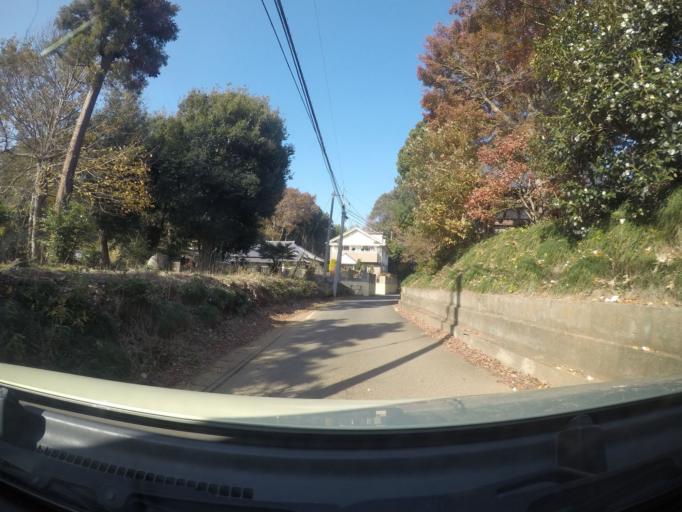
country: JP
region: Ibaraki
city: Naka
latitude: 36.0968
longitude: 140.1142
